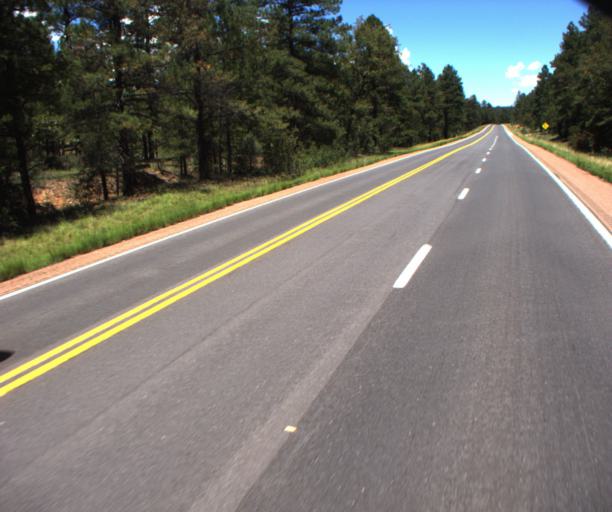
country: US
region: Arizona
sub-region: Navajo County
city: Show Low
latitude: 34.1861
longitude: -110.0921
